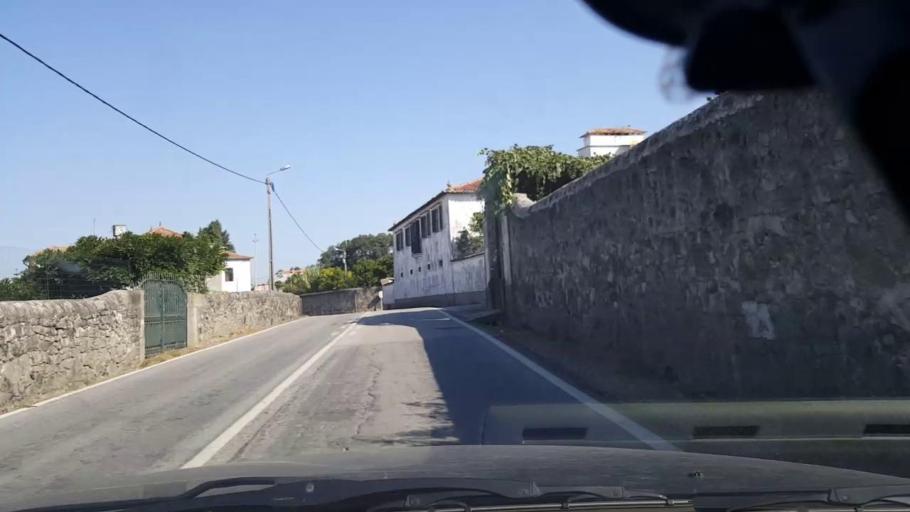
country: PT
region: Porto
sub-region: Vila do Conde
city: Arvore
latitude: 41.3705
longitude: -8.6686
